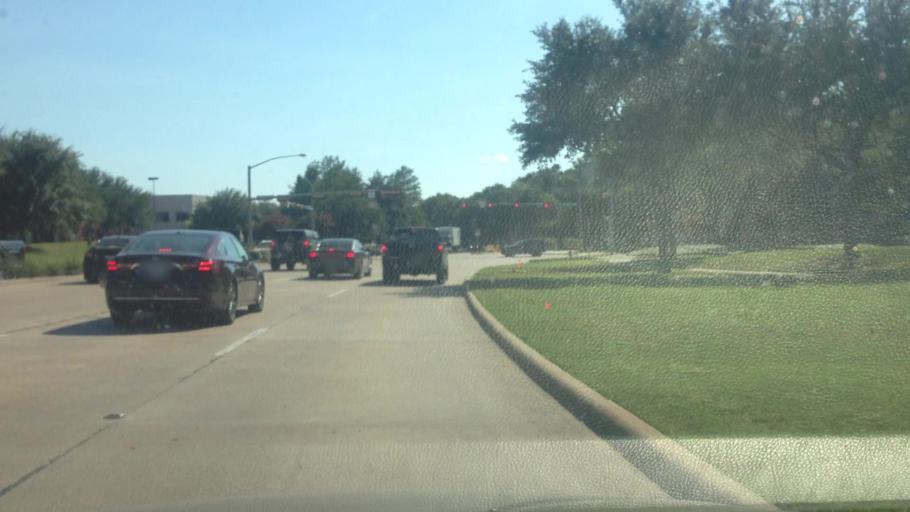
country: US
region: Texas
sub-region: Dallas County
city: Coppell
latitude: 32.9285
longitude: -97.0104
